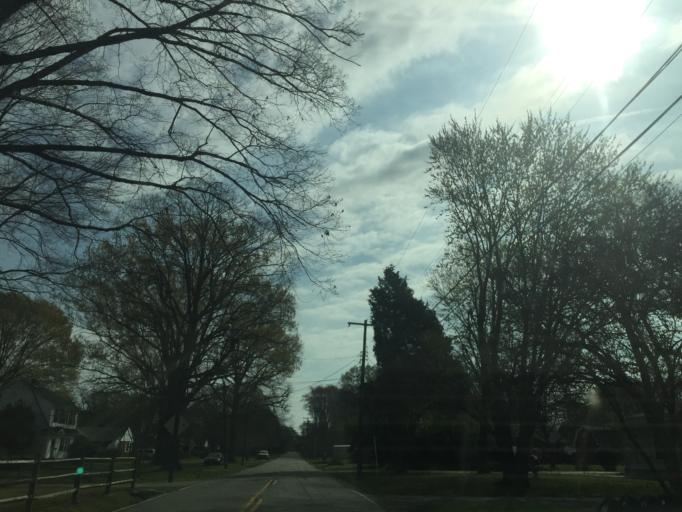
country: US
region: Virginia
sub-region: City of Newport News
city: Newport News
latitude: 37.0711
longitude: -76.4671
